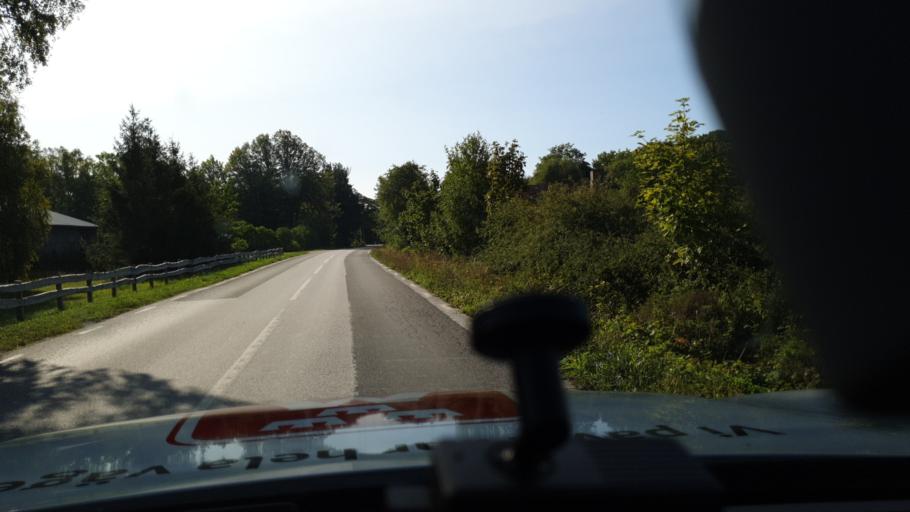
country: SE
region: Gotland
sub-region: Gotland
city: Hemse
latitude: 57.0958
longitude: 18.3038
